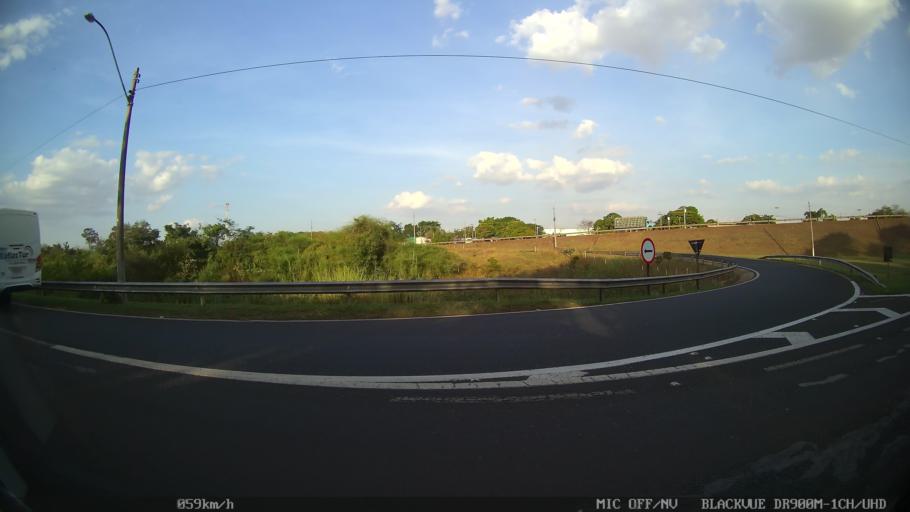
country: BR
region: Sao Paulo
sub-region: Ribeirao Preto
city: Ribeirao Preto
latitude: -21.1057
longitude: -47.8099
